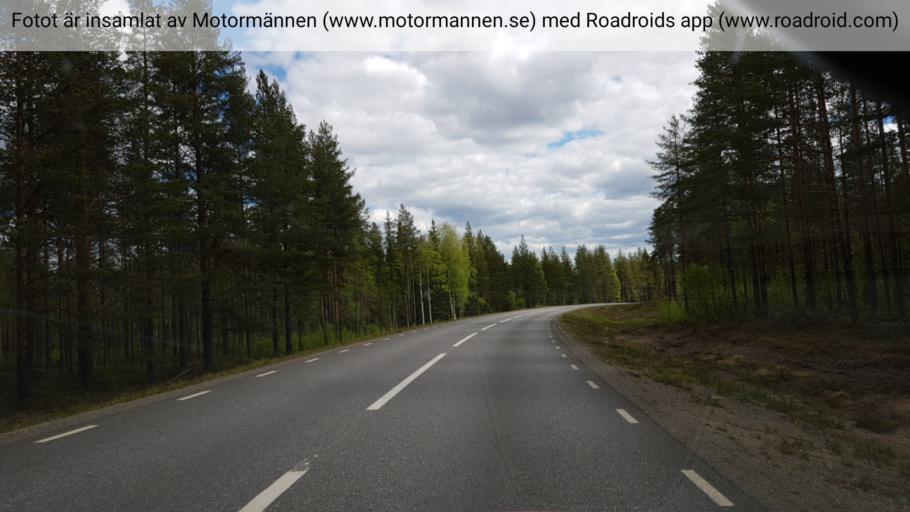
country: SE
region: Vaesterbotten
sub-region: Skelleftea Kommun
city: Langsele
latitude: 64.8190
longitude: 19.9768
